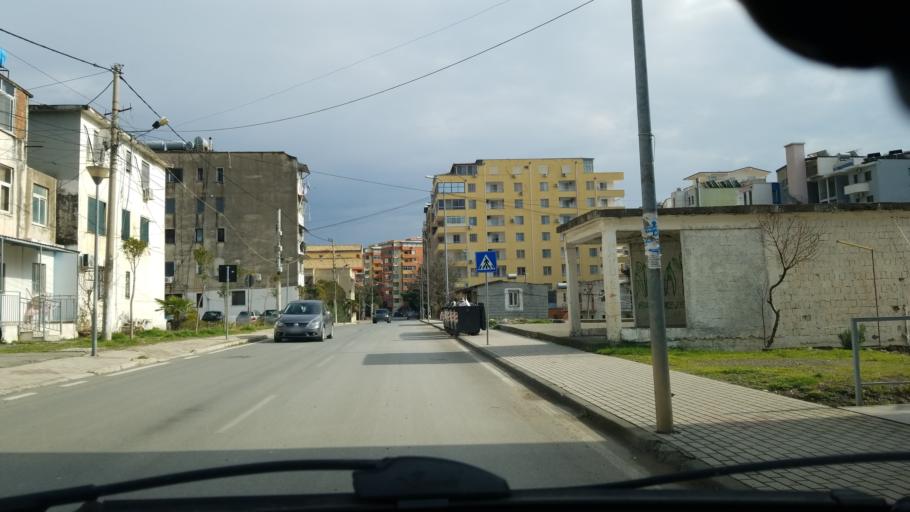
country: AL
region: Lezhe
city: Shengjin
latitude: 41.8114
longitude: 19.5967
